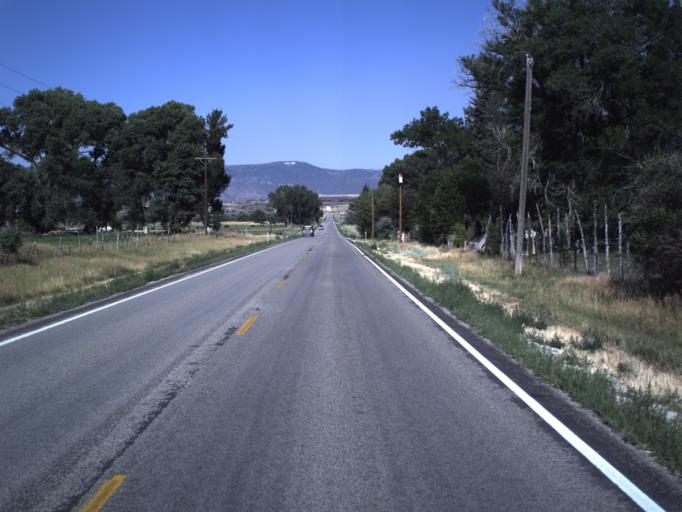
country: US
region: Utah
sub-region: Sanpete County
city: Mount Pleasant
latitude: 39.5468
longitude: -111.5065
